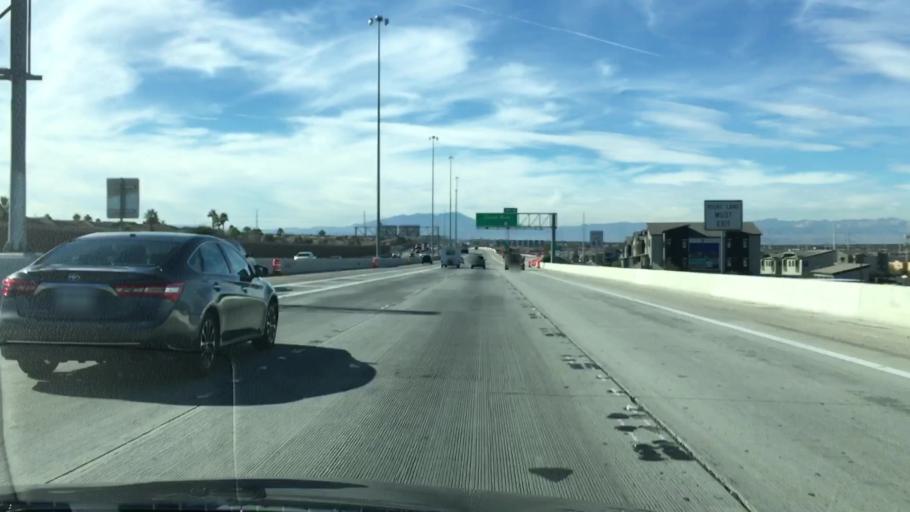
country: US
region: Nevada
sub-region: Clark County
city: Henderson
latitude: 36.0330
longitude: -115.0223
